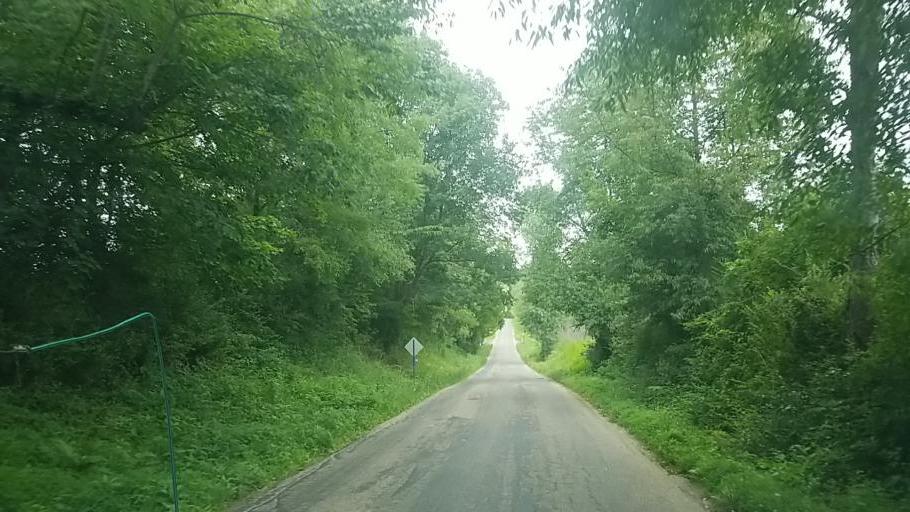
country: US
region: Ohio
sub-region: Licking County
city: Utica
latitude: 40.2409
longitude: -82.3367
